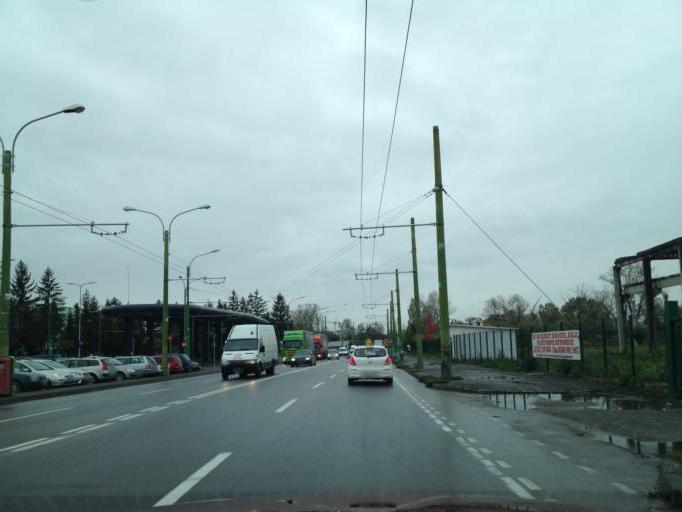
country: RO
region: Brasov
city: Brasov
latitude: 45.6811
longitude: 25.6150
